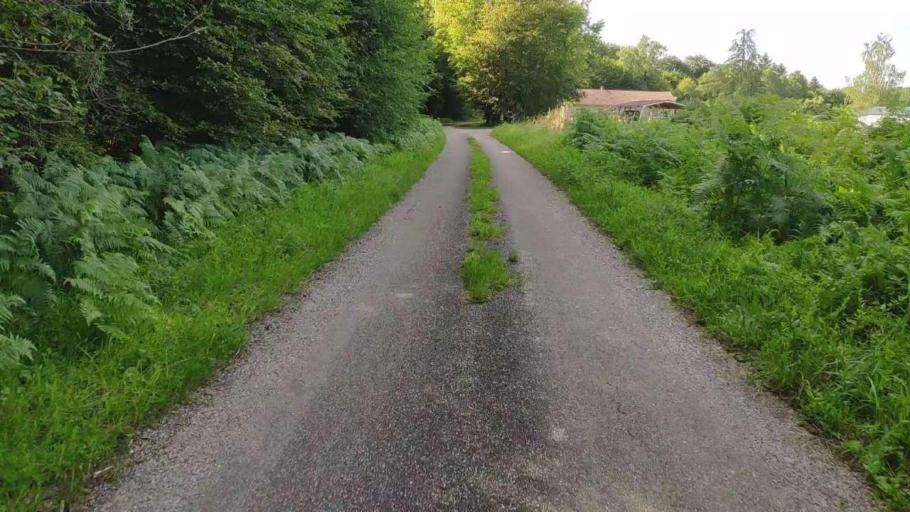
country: FR
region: Franche-Comte
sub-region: Departement du Jura
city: Bletterans
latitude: 46.8043
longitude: 5.4984
